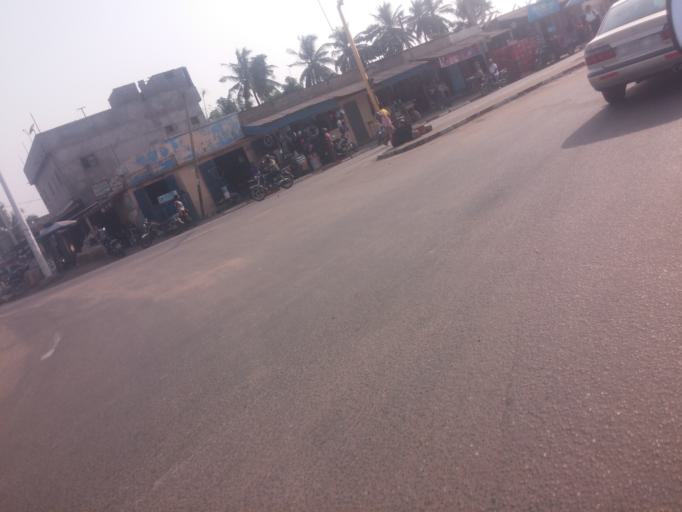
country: TG
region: Maritime
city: Lome
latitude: 6.1706
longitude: 1.2823
